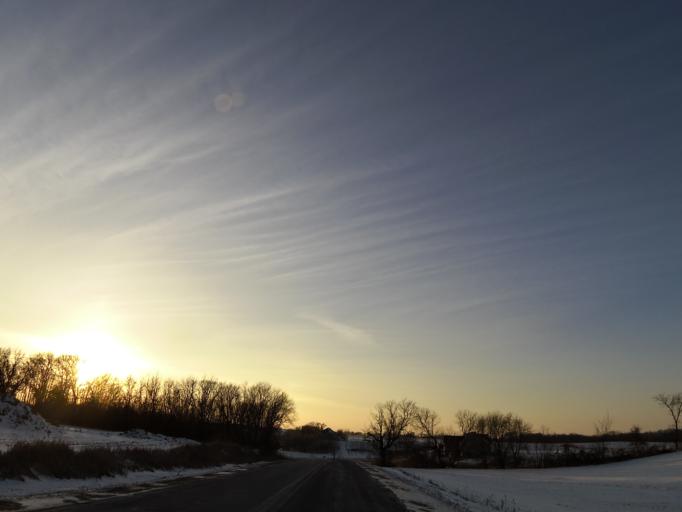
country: US
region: Wisconsin
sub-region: Pierce County
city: River Falls
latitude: 44.9163
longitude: -92.6023
